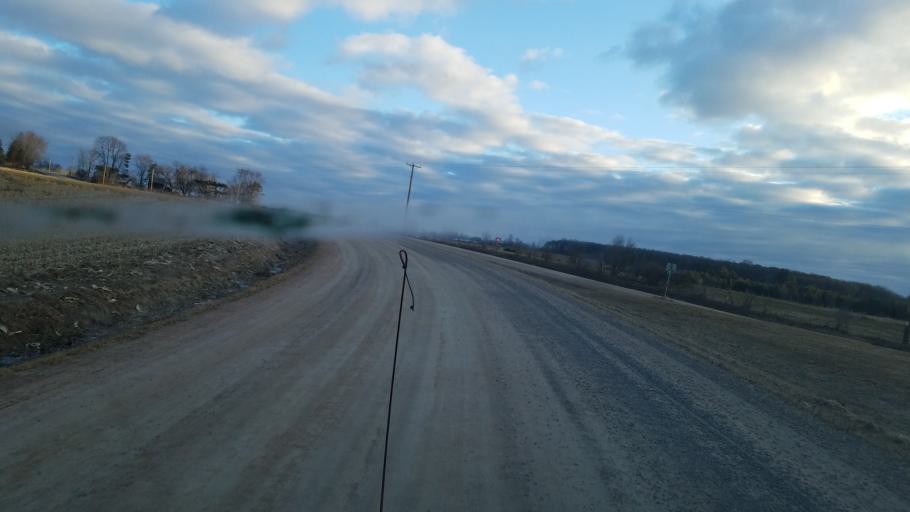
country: US
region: Wisconsin
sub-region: Clark County
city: Neillsville
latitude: 44.5970
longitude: -90.4570
